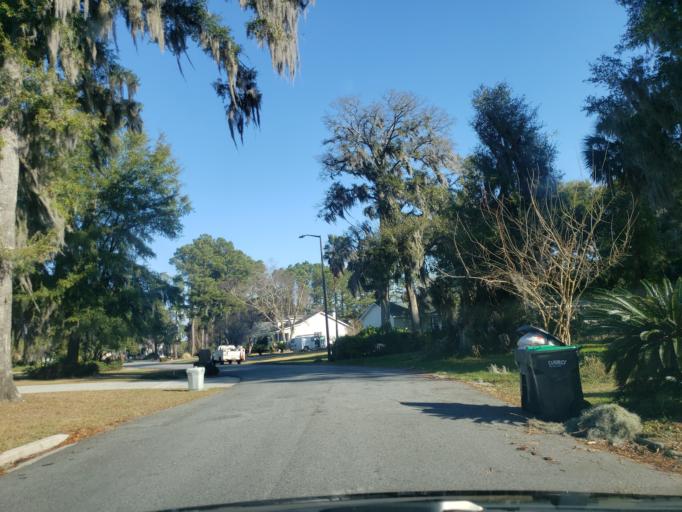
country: US
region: Georgia
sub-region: Chatham County
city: Whitemarsh Island
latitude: 32.0590
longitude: -81.0169
